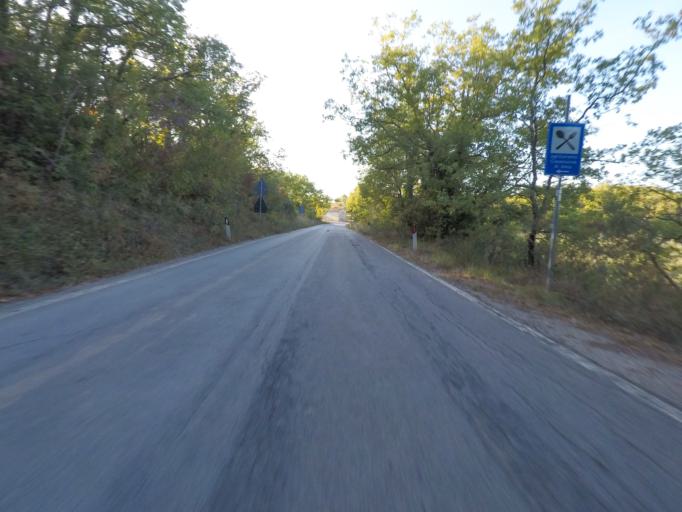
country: IT
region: Tuscany
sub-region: Provincia di Siena
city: Radda in Chianti
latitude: 43.4481
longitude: 11.3922
